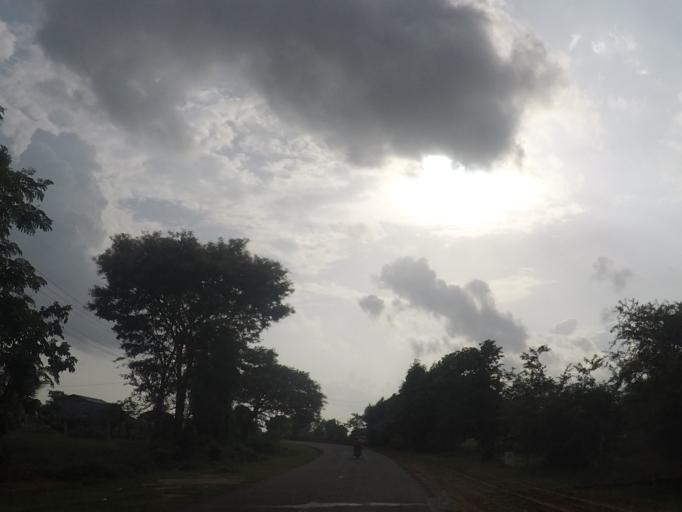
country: MM
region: Mandalay
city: Meiktila
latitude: 20.5124
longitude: 95.7488
